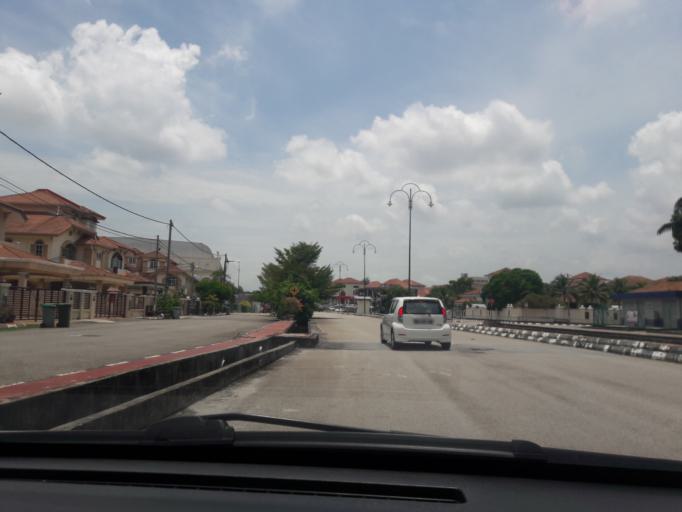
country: MY
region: Kedah
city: Sungai Petani
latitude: 5.6606
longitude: 100.4991
